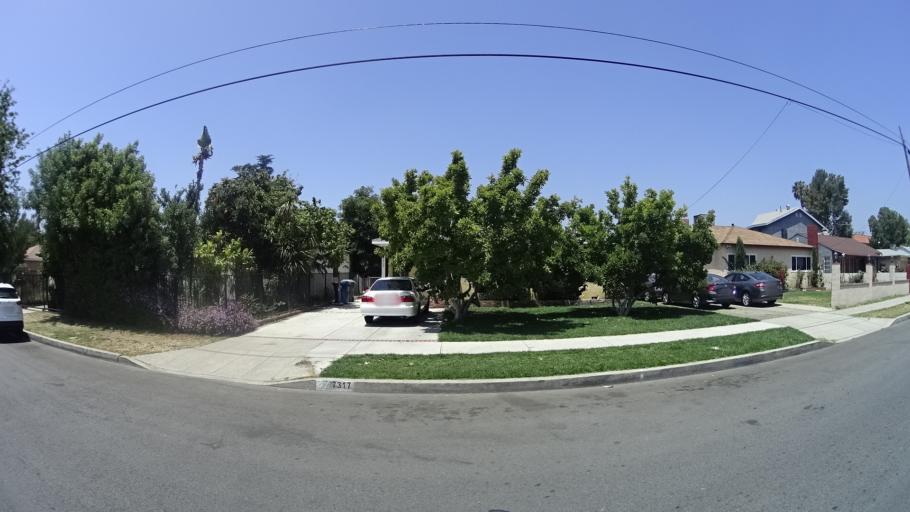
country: US
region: California
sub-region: Los Angeles County
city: Van Nuys
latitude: 34.2035
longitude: -118.4445
